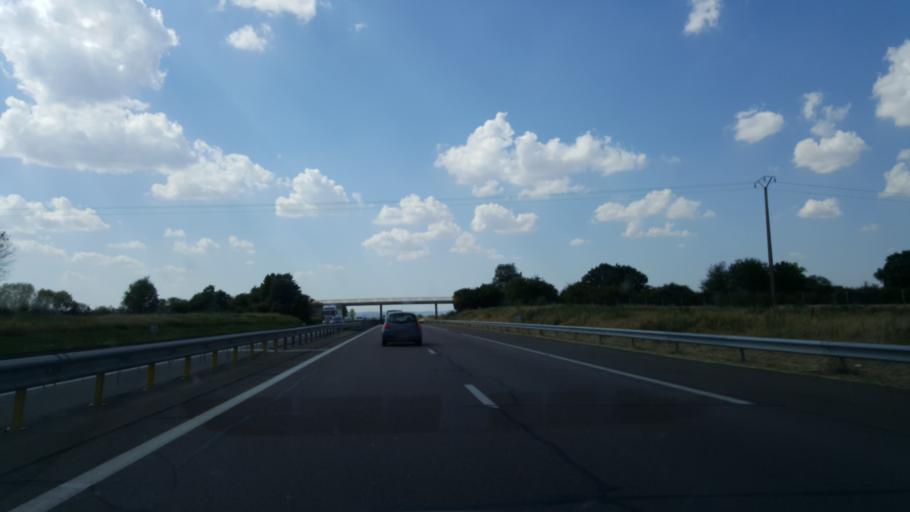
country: FR
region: Bourgogne
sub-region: Departement de la Cote-d'Or
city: Semur-en-Auxois
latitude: 47.4742
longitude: 4.2072
